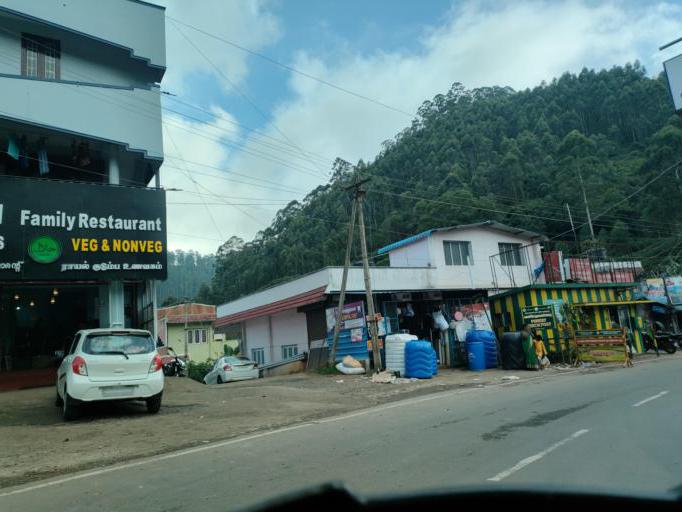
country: IN
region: Tamil Nadu
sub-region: Dindigul
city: Kodaikanal
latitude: 10.2649
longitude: 77.5394
